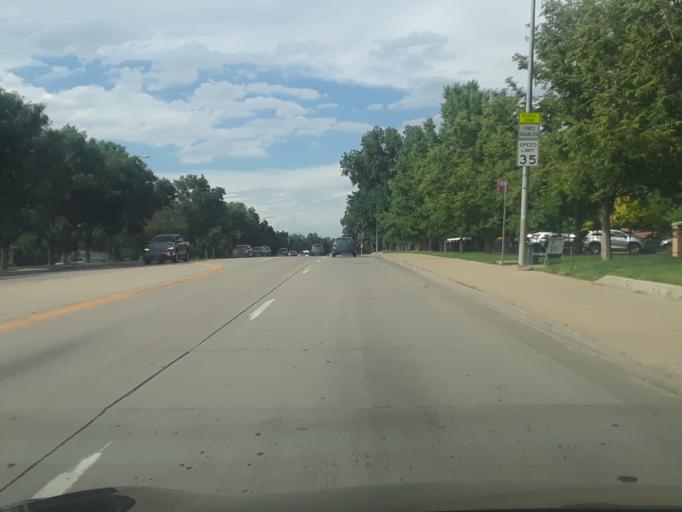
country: US
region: Colorado
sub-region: Arapahoe County
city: Glendale
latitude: 39.7216
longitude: -104.9035
